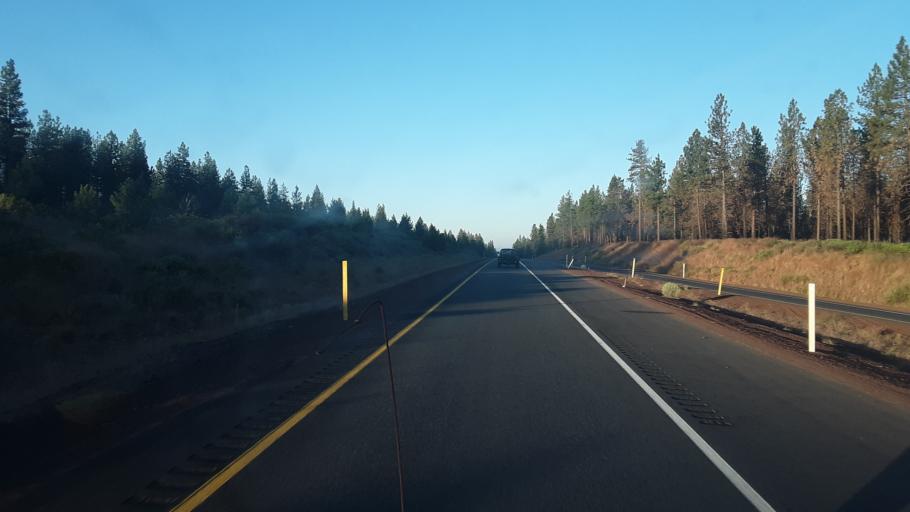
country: US
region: Oregon
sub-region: Deschutes County
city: Sunriver
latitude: 43.8677
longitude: -121.4046
